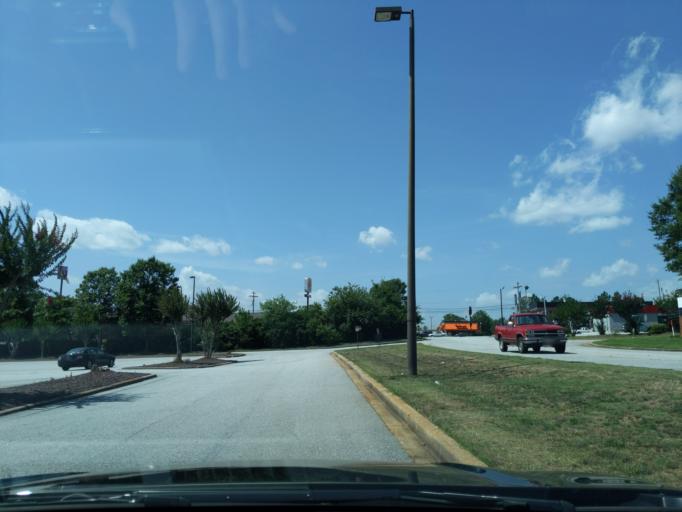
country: US
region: South Carolina
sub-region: Spartanburg County
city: Saxon
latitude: 34.9836
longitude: -81.9693
